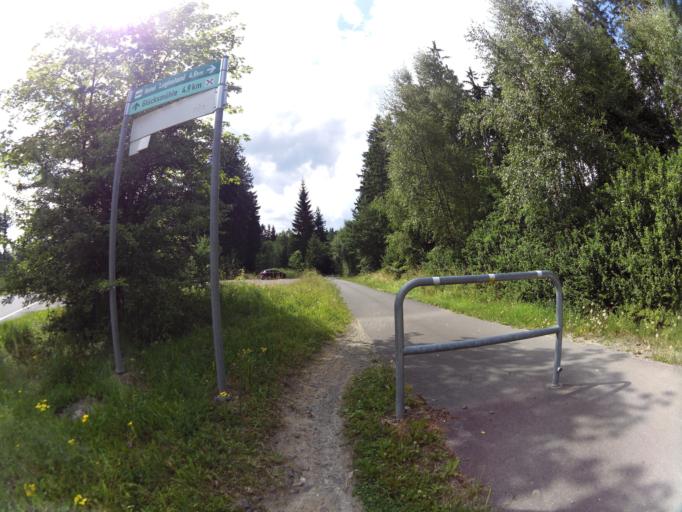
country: DE
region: Thuringia
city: Burgk
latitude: 50.5496
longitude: 11.7537
